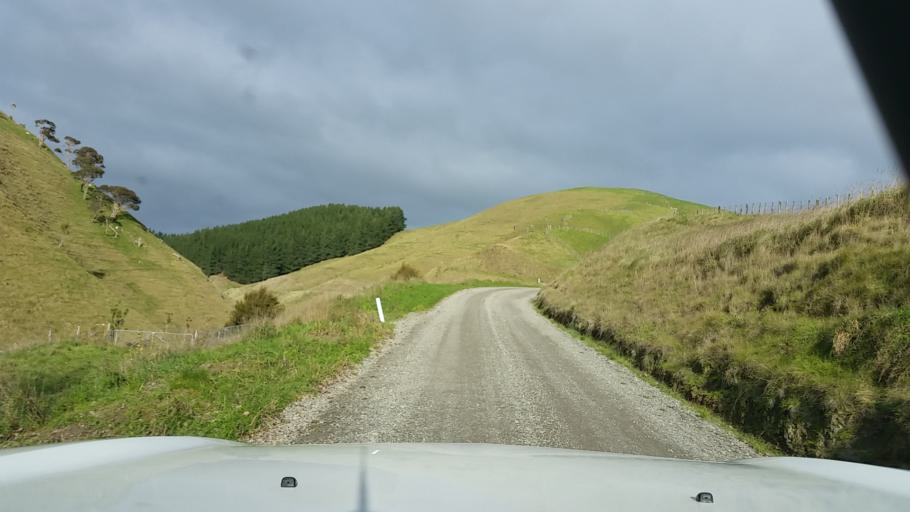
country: NZ
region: Wellington
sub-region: Masterton District
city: Masterton
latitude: -41.0351
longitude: 175.7127
